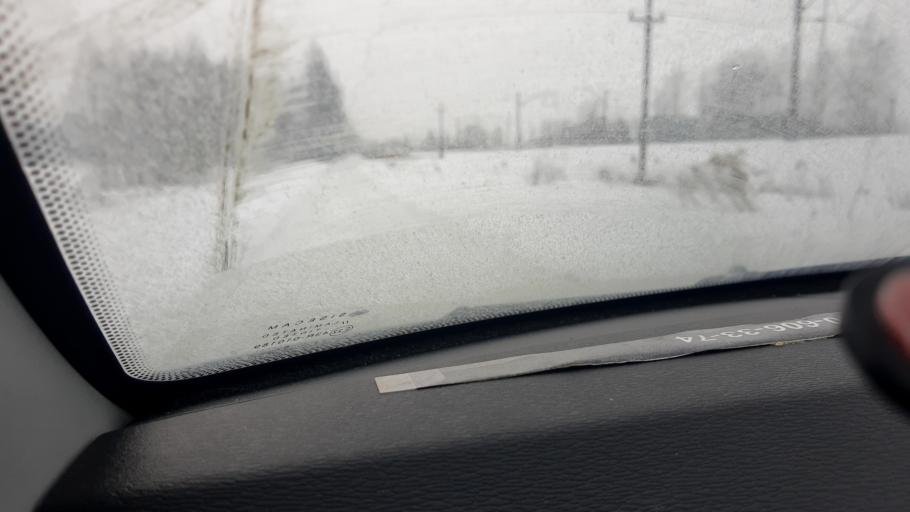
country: RU
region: Nizjnij Novgorod
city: Sitniki
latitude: 56.5272
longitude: 44.0539
